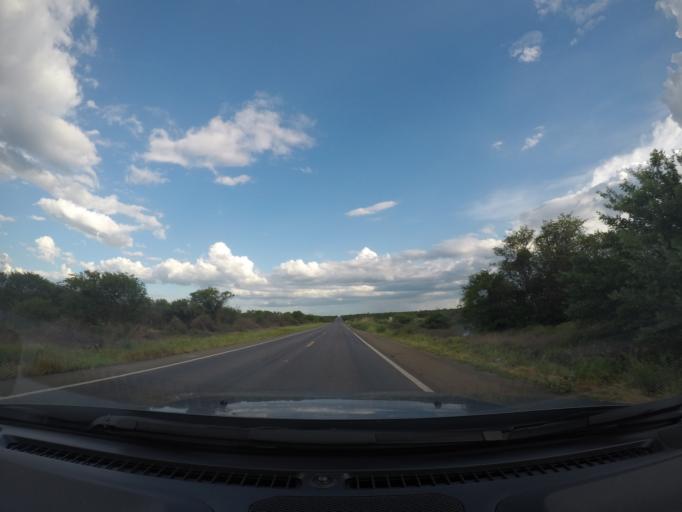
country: BR
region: Bahia
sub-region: Oliveira Dos Brejinhos
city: Beira Rio
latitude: -12.1944
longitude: -42.8197
